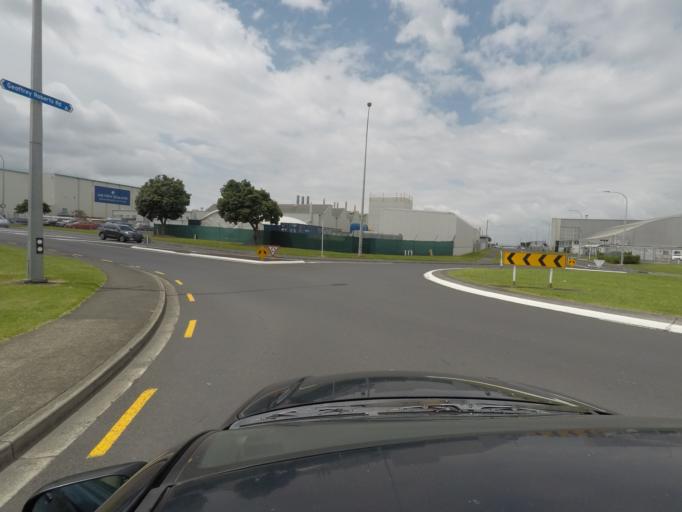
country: NZ
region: Auckland
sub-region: Auckland
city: Mangere
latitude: -37.0020
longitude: 174.7949
